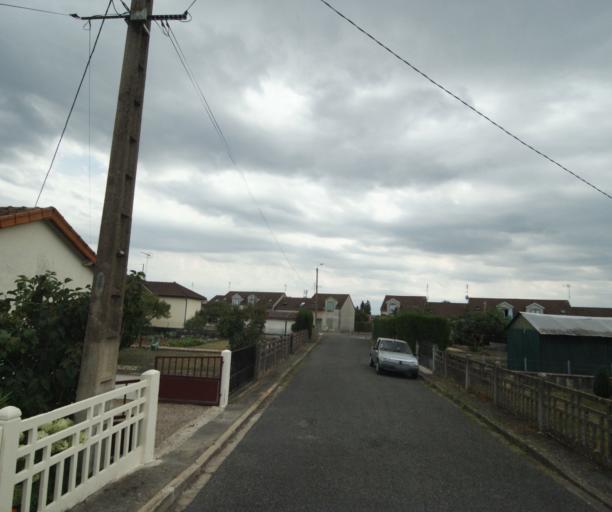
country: FR
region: Bourgogne
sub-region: Departement de Saone-et-Loire
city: Gueugnon
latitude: 46.6062
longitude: 4.0571
